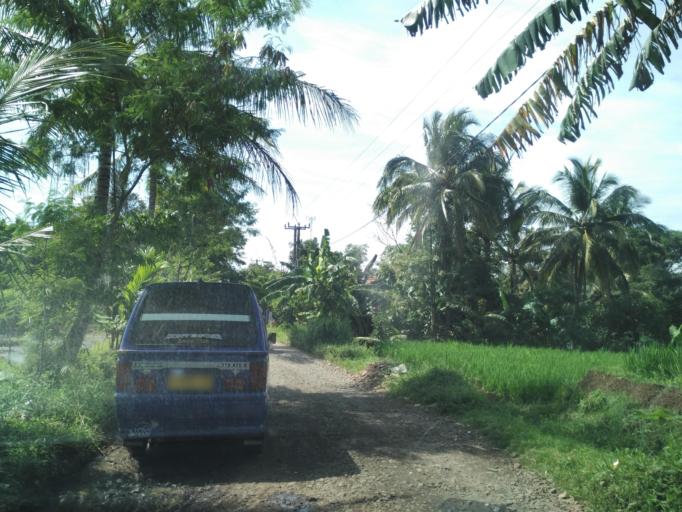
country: ID
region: West Java
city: Cibeber
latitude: -6.8398
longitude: 107.0829
